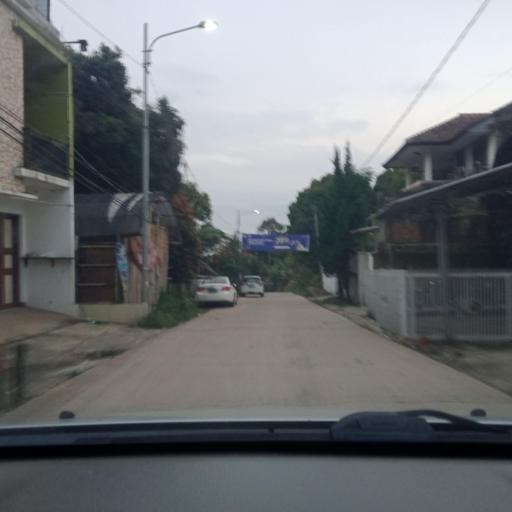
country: ID
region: West Java
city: Lembang
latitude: -6.8311
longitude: 107.5857
